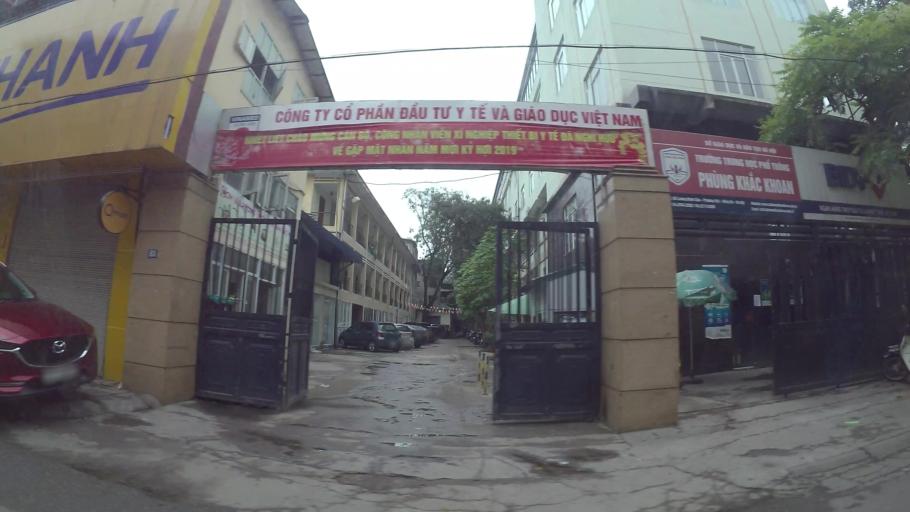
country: VN
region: Ha Noi
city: Hai BaTrung
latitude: 21.0027
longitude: 105.8360
